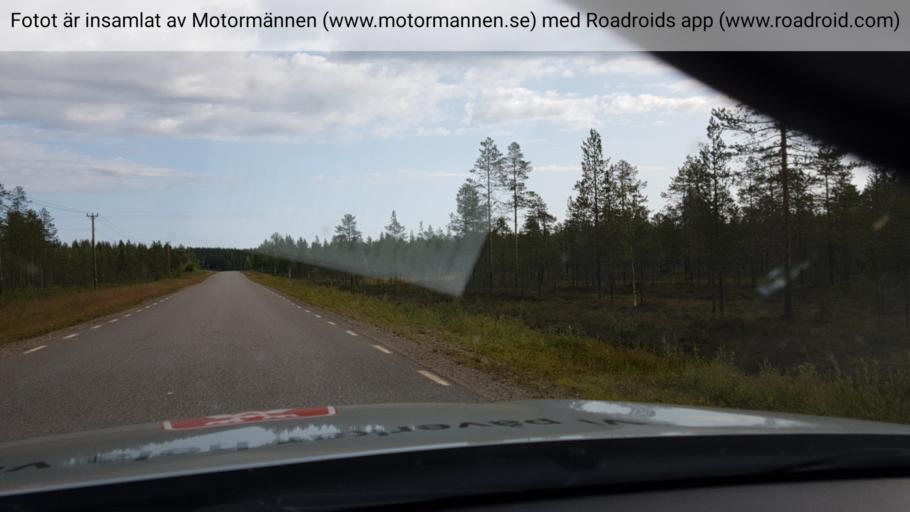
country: SE
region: Vaesterbotten
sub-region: Skelleftea Kommun
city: Storvik
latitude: 65.4256
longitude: 20.3941
